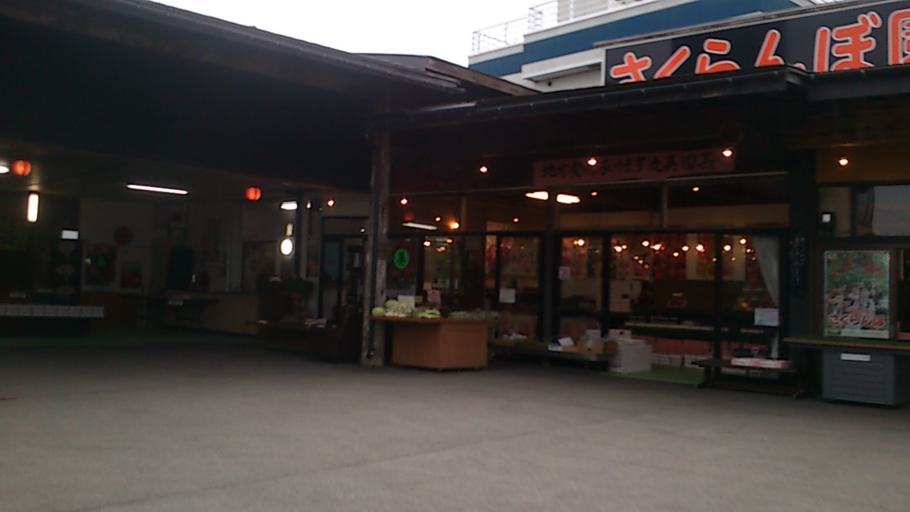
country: JP
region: Yamagata
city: Higashine
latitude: 38.4247
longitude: 140.3763
